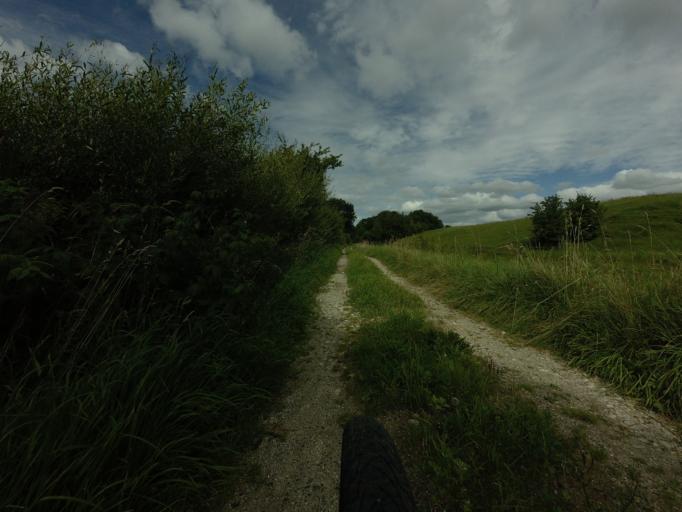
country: DK
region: Central Jutland
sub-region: Syddjurs Kommune
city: Ryomgard
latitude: 56.3941
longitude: 10.5316
